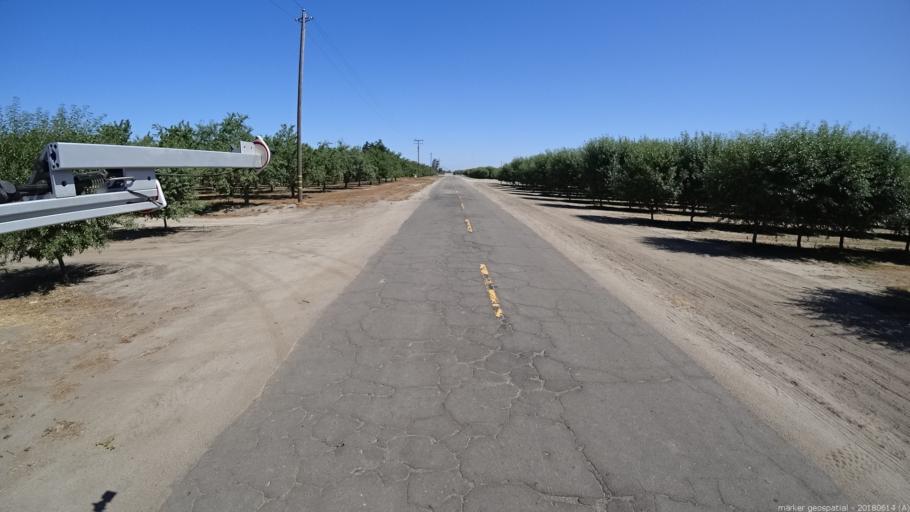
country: US
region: California
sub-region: Madera County
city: Fairmead
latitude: 36.9648
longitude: -120.2204
